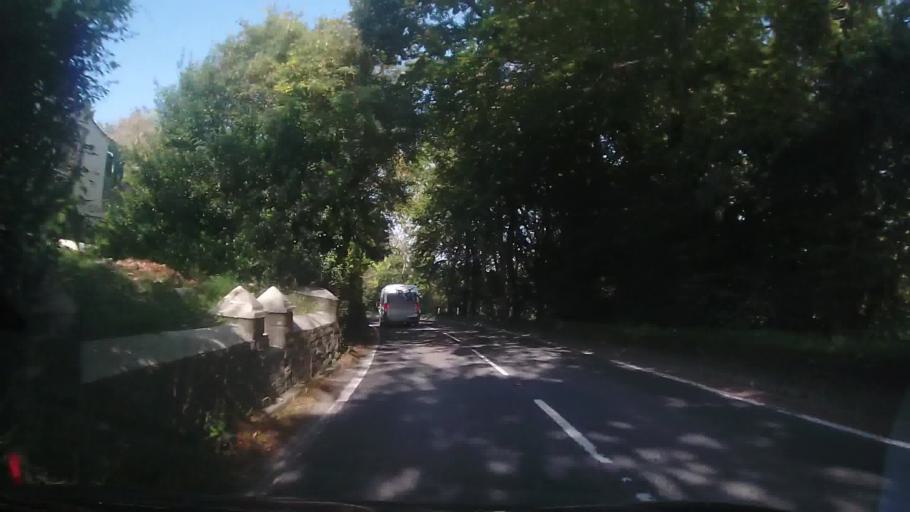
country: GB
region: Wales
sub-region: County of Ceredigion
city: Cardigan
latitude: 52.0648
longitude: -4.6810
